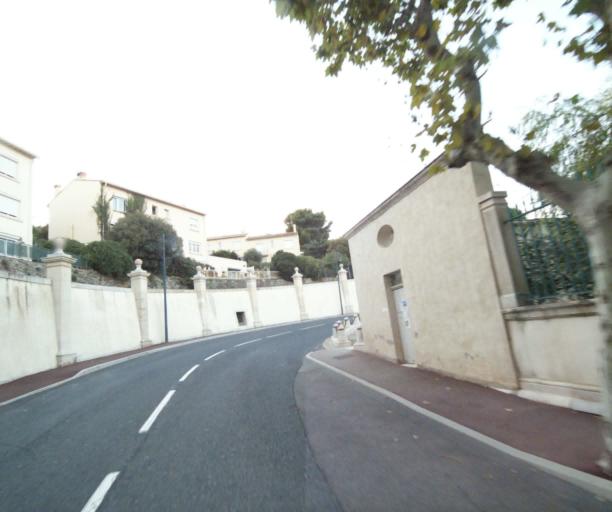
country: FR
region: Languedoc-Roussillon
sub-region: Departement des Pyrenees-Orientales
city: Portvendres
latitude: 42.5209
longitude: 3.1055
